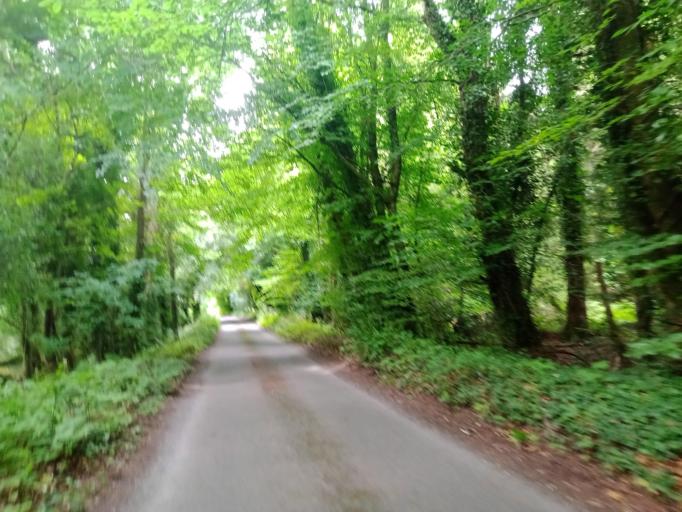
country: IE
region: Leinster
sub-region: Laois
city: Abbeyleix
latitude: 52.9001
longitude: -7.3612
